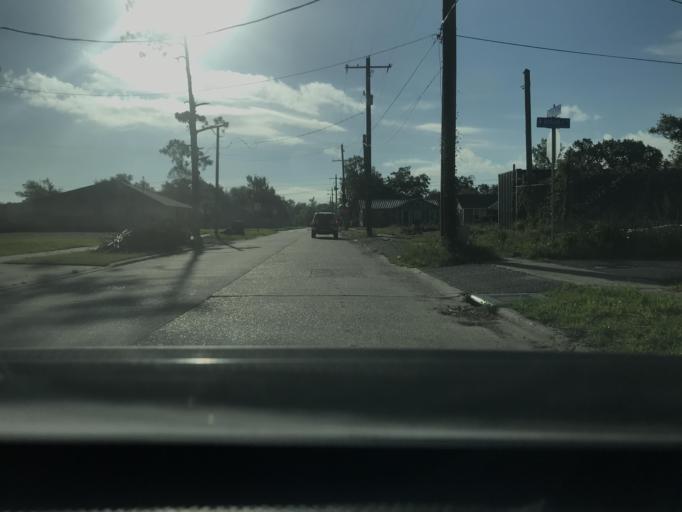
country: US
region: Louisiana
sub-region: Calcasieu Parish
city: Lake Charles
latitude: 30.2069
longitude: -93.2168
